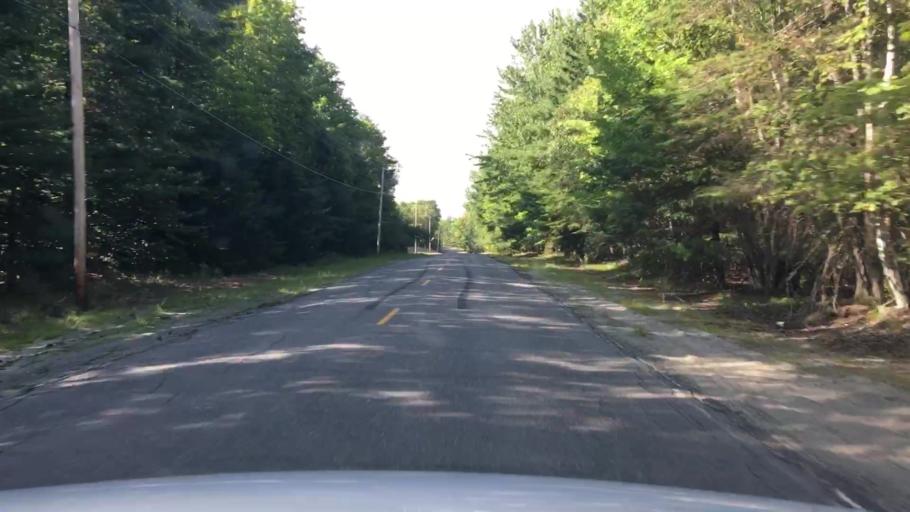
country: US
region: Maine
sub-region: Penobscot County
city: Enfield
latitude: 45.2208
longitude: -68.5366
